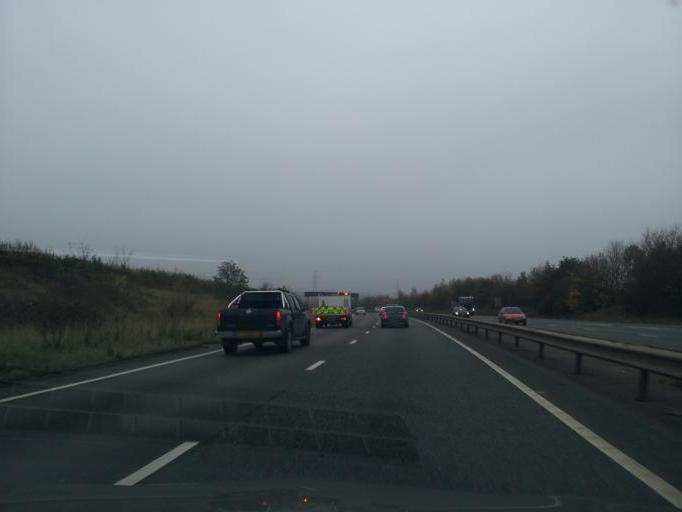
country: GB
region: England
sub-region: Leicestershire
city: Kirby Muxloe
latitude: 52.6537
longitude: -1.2189
